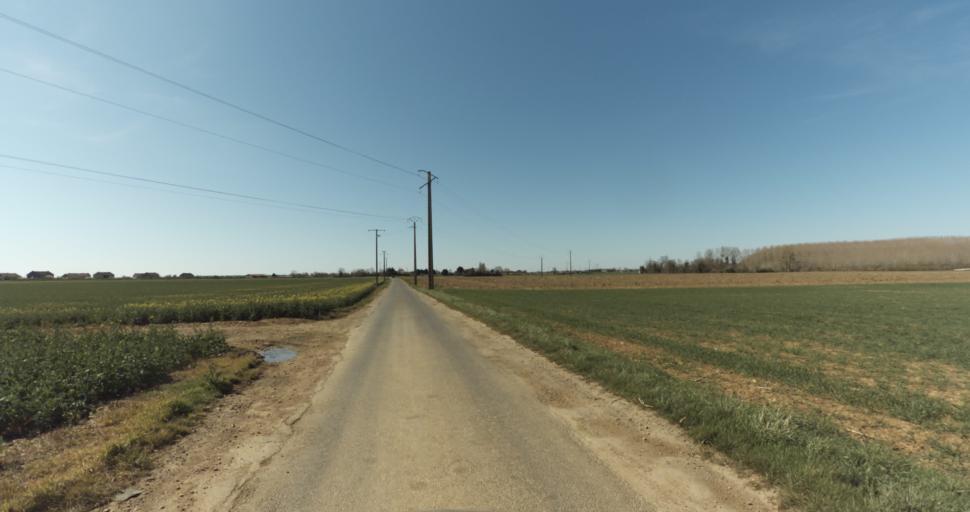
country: FR
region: Lower Normandy
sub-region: Departement du Calvados
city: Saint-Pierre-sur-Dives
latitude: 49.0508
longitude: -0.0398
